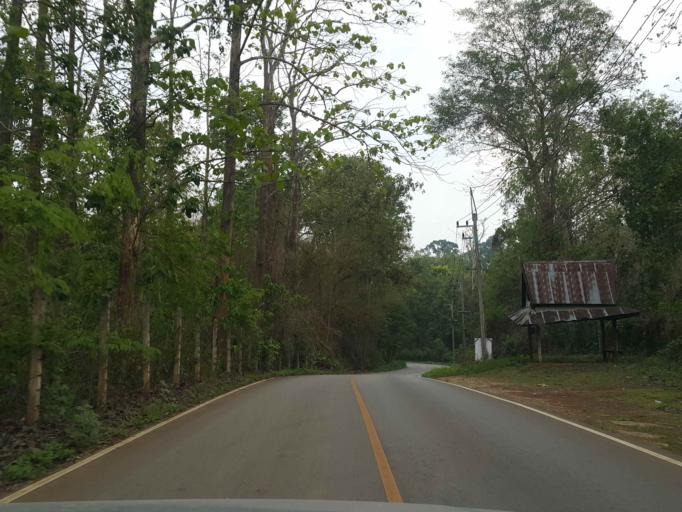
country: TH
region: Chiang Mai
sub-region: Amphoe Chiang Dao
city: Chiang Dao
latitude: 19.3850
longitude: 98.9362
